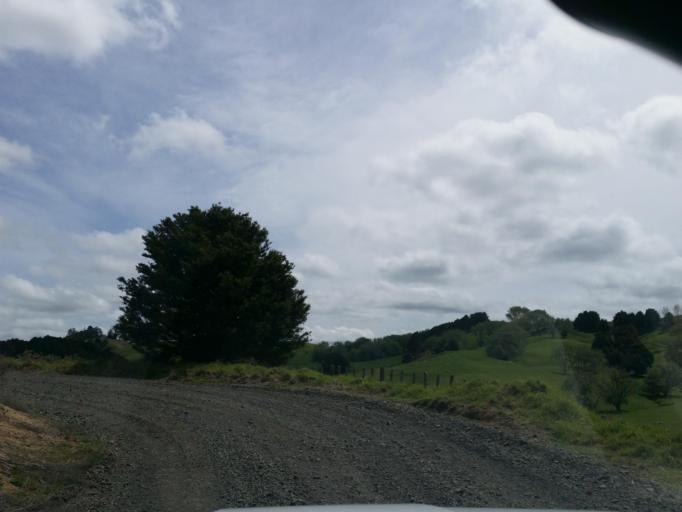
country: NZ
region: Northland
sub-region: Kaipara District
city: Dargaville
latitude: -35.9192
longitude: 174.0827
